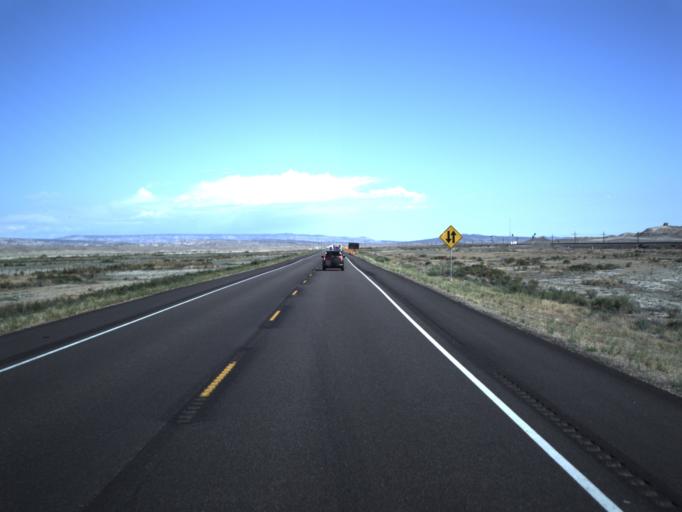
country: US
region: Utah
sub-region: Carbon County
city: East Carbon City
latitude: 39.0105
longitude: -110.2820
